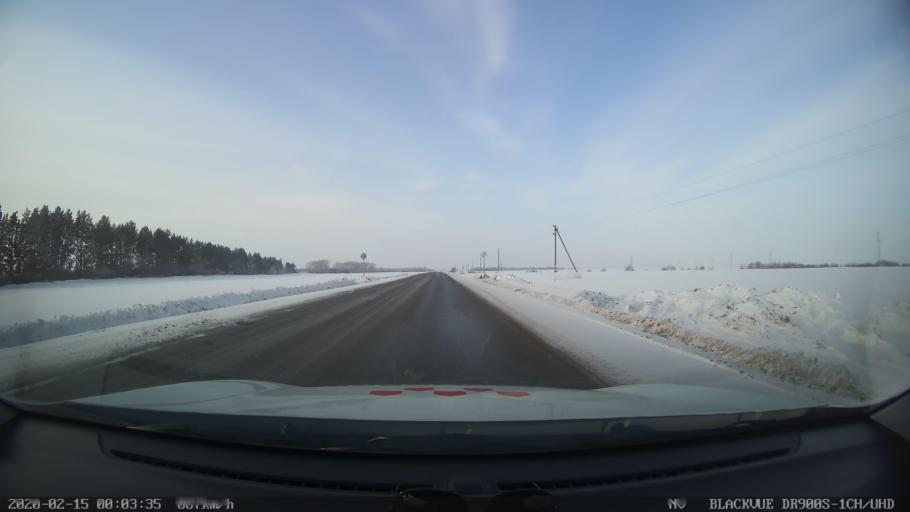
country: RU
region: Tatarstan
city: Kuybyshevskiy Zaton
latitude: 55.3735
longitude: 48.9958
